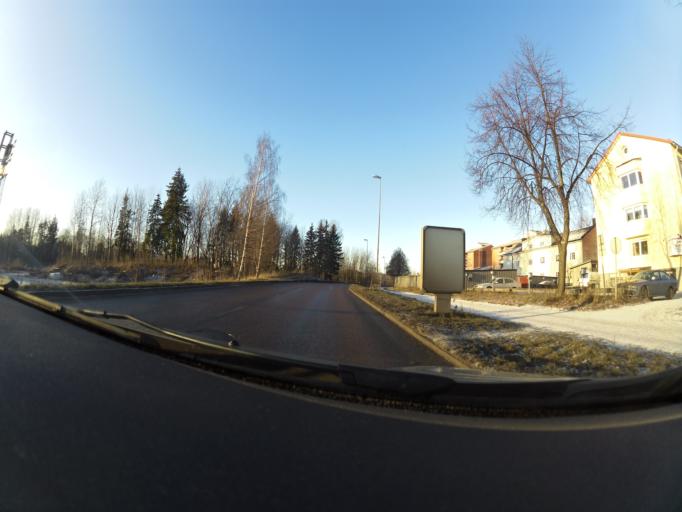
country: SE
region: Gaevleborg
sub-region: Gavle Kommun
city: Gavle
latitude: 60.6676
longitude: 17.1641
